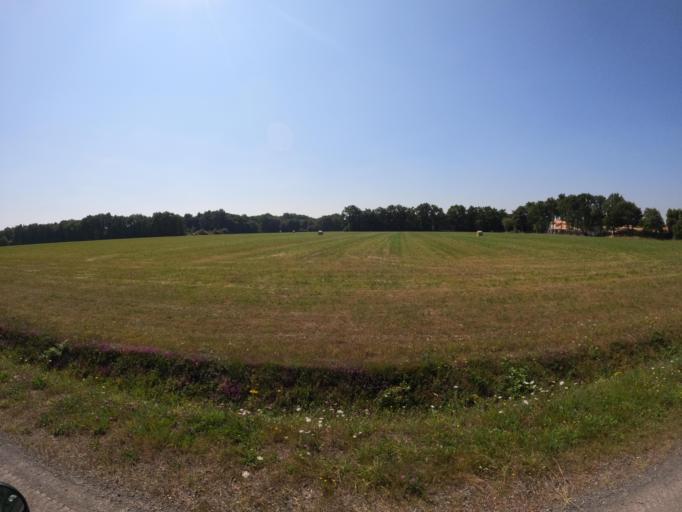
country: FR
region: Pays de la Loire
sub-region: Departement de la Loire-Atlantique
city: Geneston
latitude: 47.0660
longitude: -1.5122
